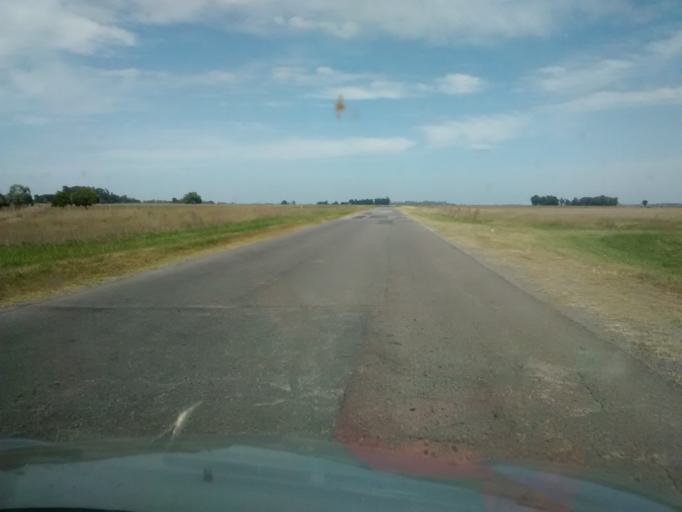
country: AR
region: Buenos Aires
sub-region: Partido de Ayacucho
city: Ayacucho
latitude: -37.1343
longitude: -58.5526
